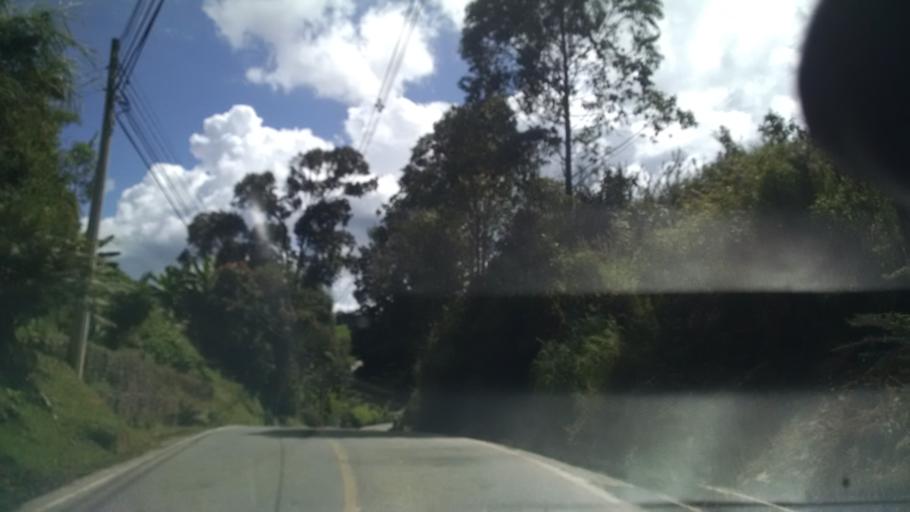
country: CO
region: Antioquia
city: El Retiro
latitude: 6.0890
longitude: -75.5026
